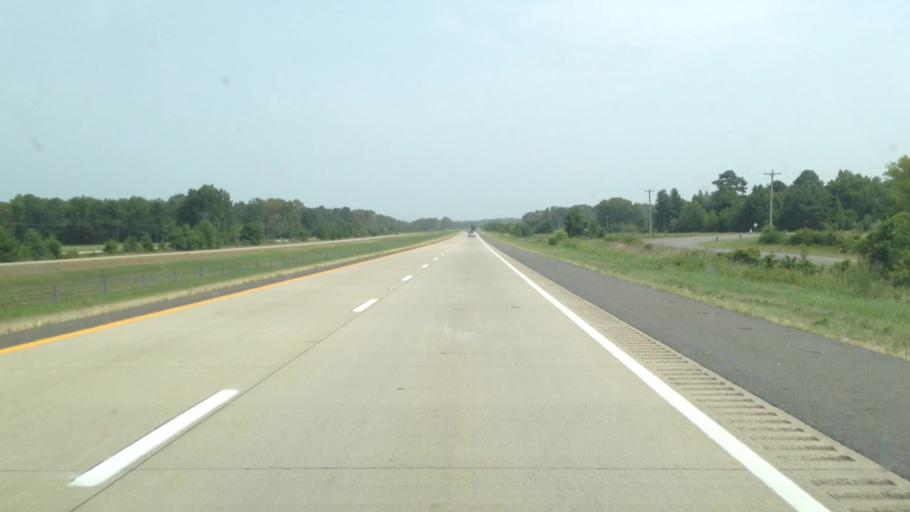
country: US
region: Texas
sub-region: Cass County
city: Queen City
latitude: 33.1839
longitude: -93.8776
